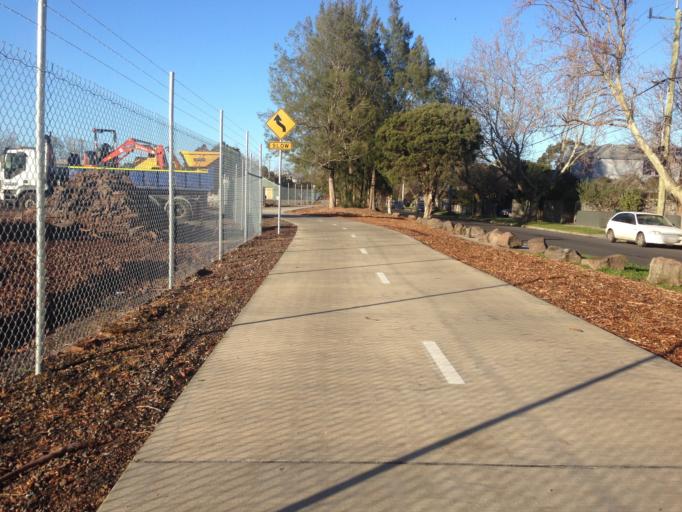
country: AU
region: Victoria
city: Alphington
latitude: -37.7764
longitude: 145.0318
